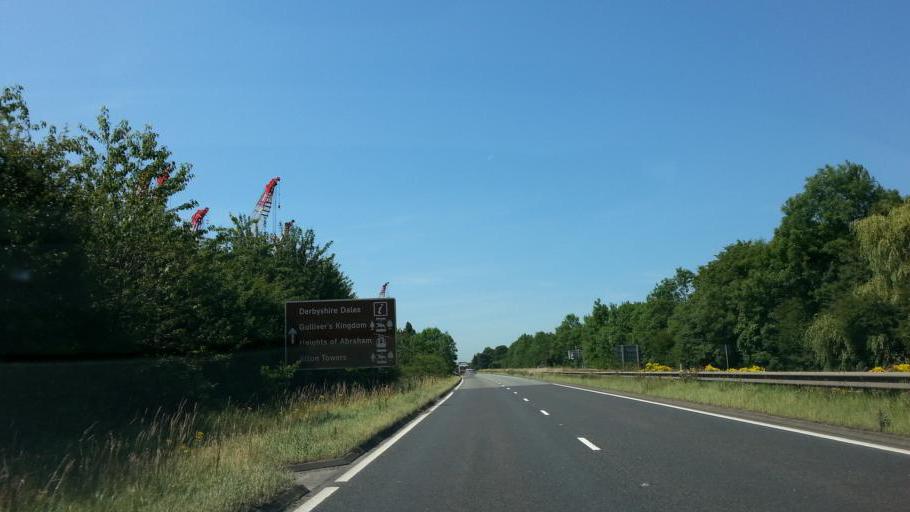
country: GB
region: England
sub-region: Derbyshire
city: Alfreton
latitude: 53.0924
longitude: -1.3627
